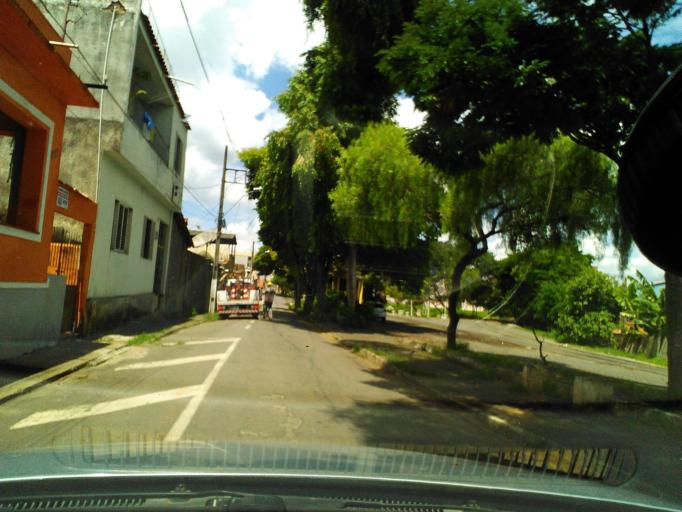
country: BR
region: Minas Gerais
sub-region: Tres Coracoes
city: Tres Coracoes
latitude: -21.6959
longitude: -45.2632
